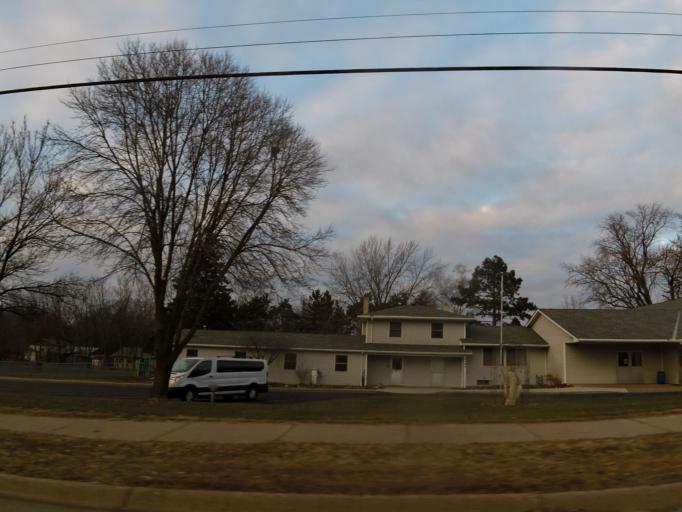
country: US
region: Minnesota
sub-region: Washington County
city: Birchwood
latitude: 45.0502
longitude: -92.9980
